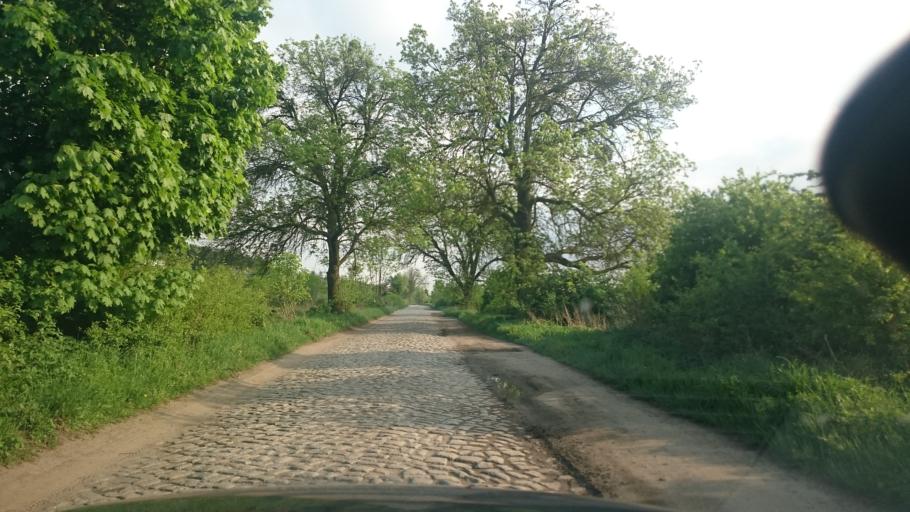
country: PL
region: Kujawsko-Pomorskie
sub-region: Grudziadz
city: Grudziadz
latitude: 53.4770
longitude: 18.8136
